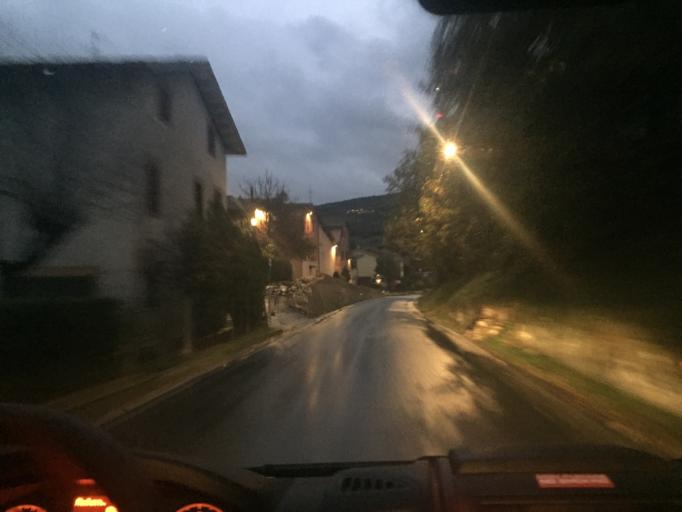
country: IT
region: The Marches
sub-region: Provincia di Macerata
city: Muccia
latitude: 43.0859
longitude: 13.0449
